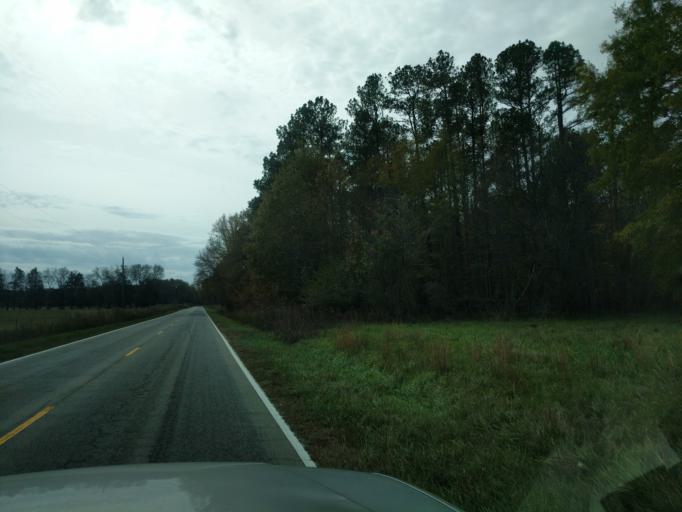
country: US
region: South Carolina
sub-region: Laurens County
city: Joanna
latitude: 34.2956
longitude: -81.8445
